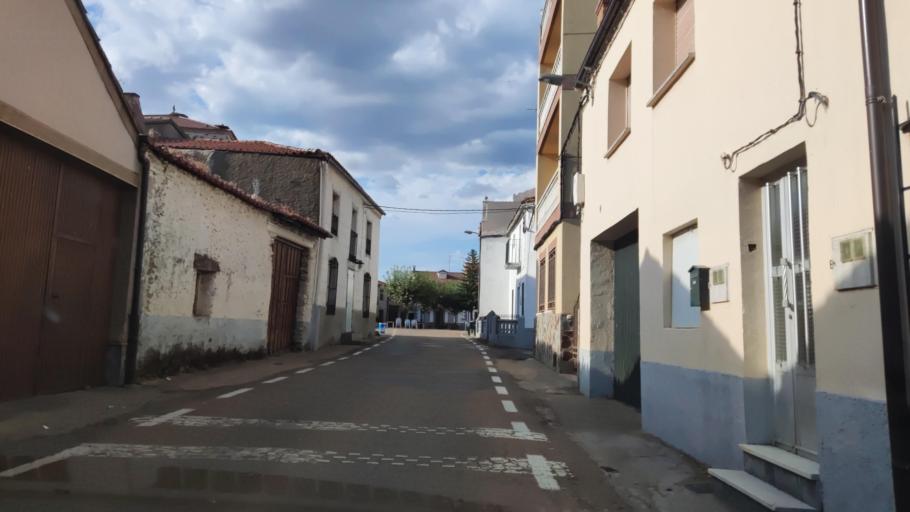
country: ES
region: Castille and Leon
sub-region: Provincia de Salamanca
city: Martiago
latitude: 40.4531
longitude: -6.4902
